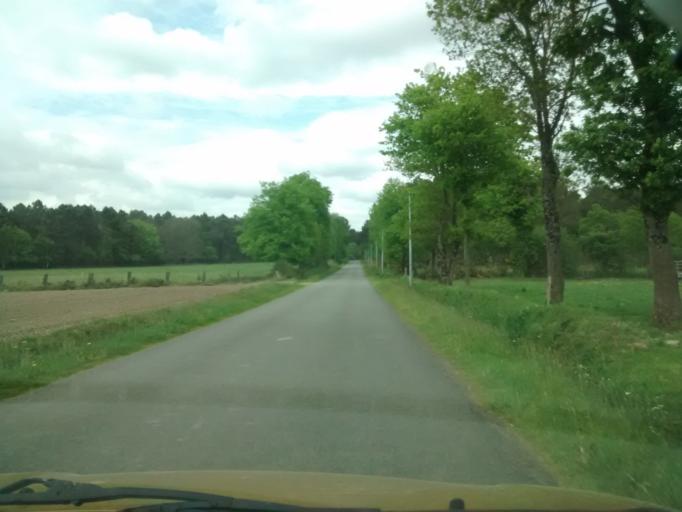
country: FR
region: Brittany
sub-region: Departement du Morbihan
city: Molac
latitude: 47.7338
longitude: -2.4230
